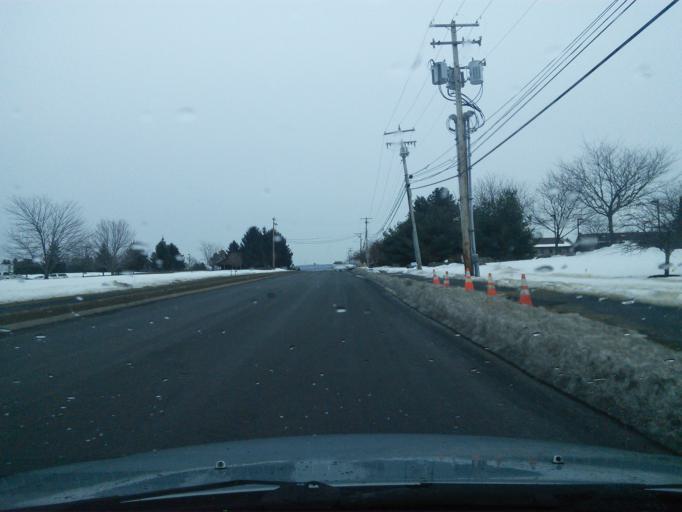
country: US
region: Pennsylvania
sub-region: Centre County
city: Pine Grove Mills
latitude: 40.7659
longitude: -77.8794
